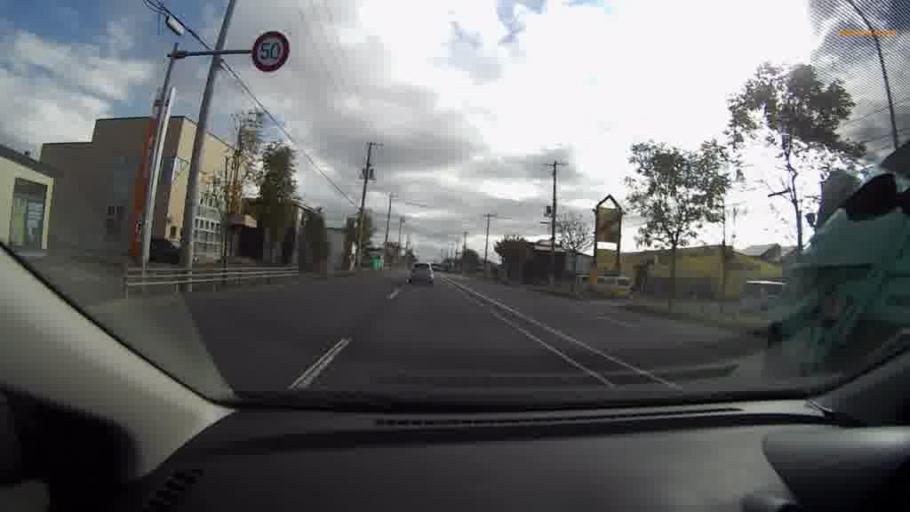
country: JP
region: Hokkaido
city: Kushiro
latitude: 43.0099
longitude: 144.2742
